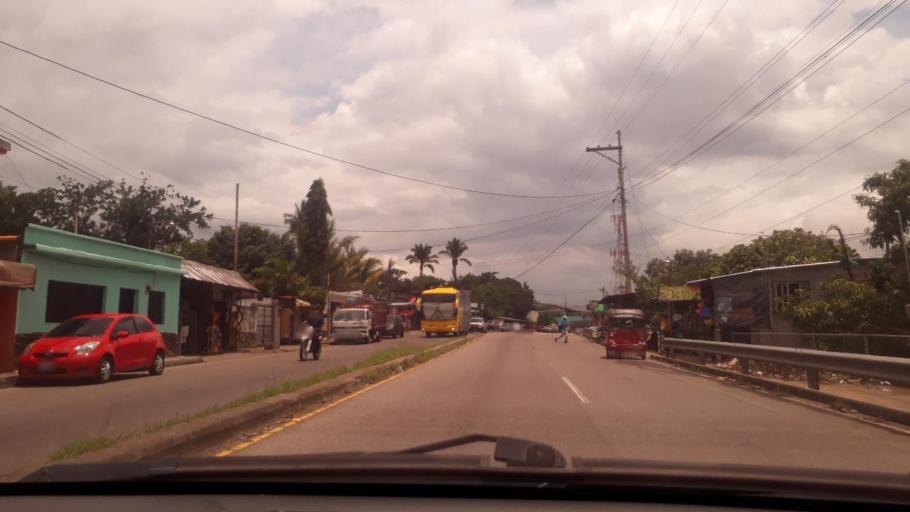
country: GT
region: Santa Rosa
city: Cuilapa
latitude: 14.2514
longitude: -90.2756
